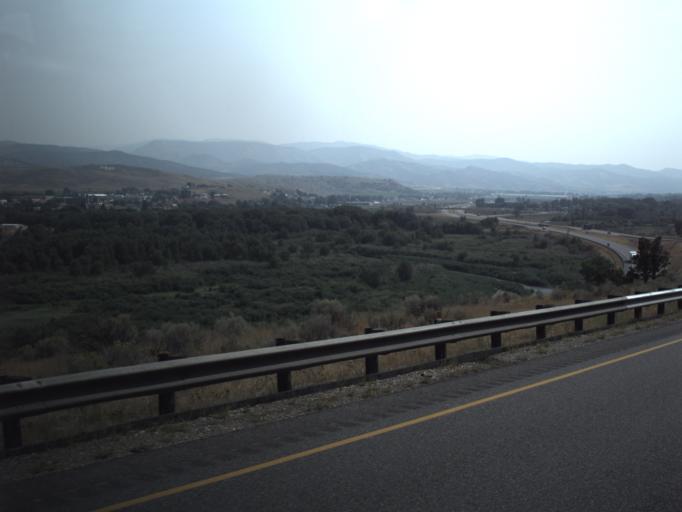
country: US
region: Utah
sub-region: Summit County
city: Coalville
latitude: 40.9255
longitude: -111.4116
